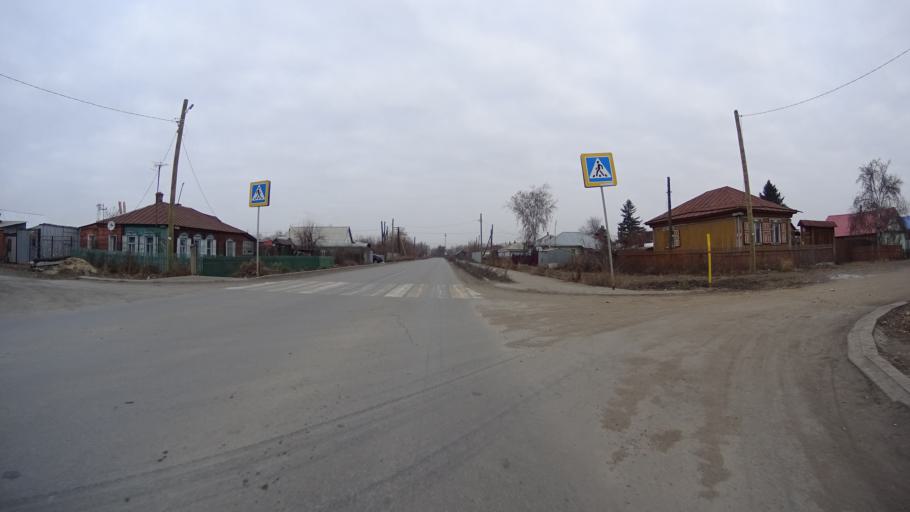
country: RU
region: Chelyabinsk
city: Troitsk
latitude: 54.1067
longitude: 61.5685
